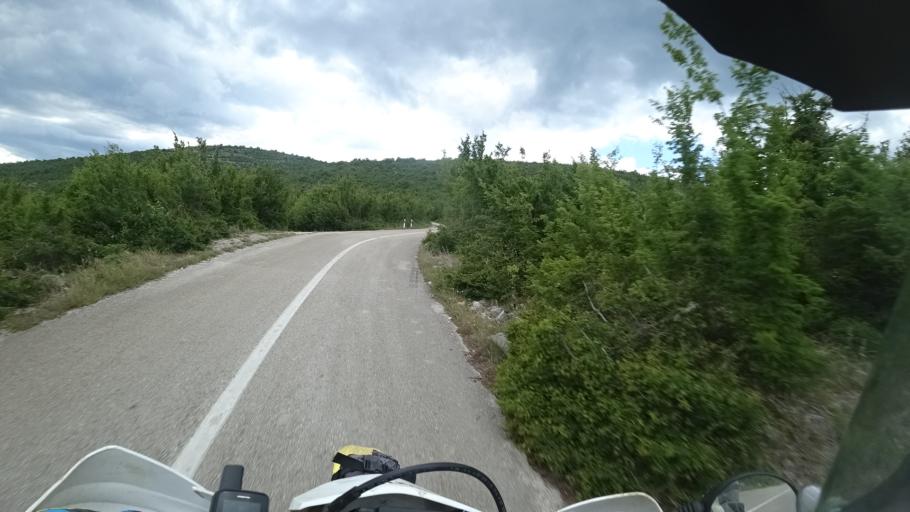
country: HR
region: Zadarska
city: Gracac
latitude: 44.1943
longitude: 15.8862
